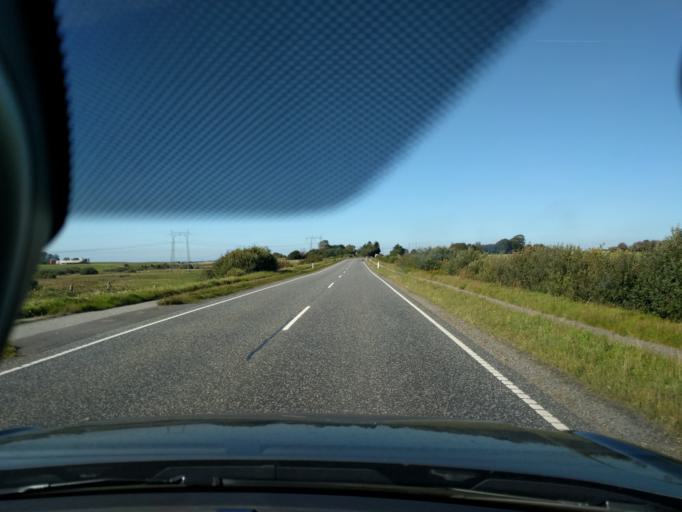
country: DK
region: North Denmark
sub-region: Vesthimmerland Kommune
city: Alestrup
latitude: 56.7146
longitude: 9.6154
